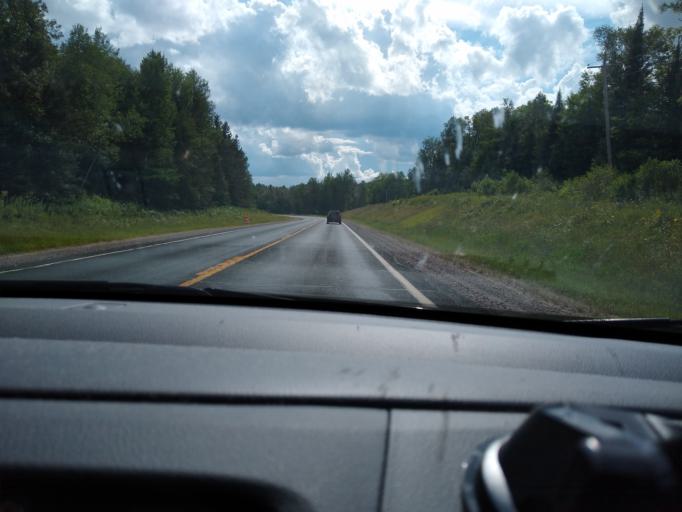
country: US
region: Michigan
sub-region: Iron County
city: Crystal Falls
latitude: 46.2841
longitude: -88.0145
